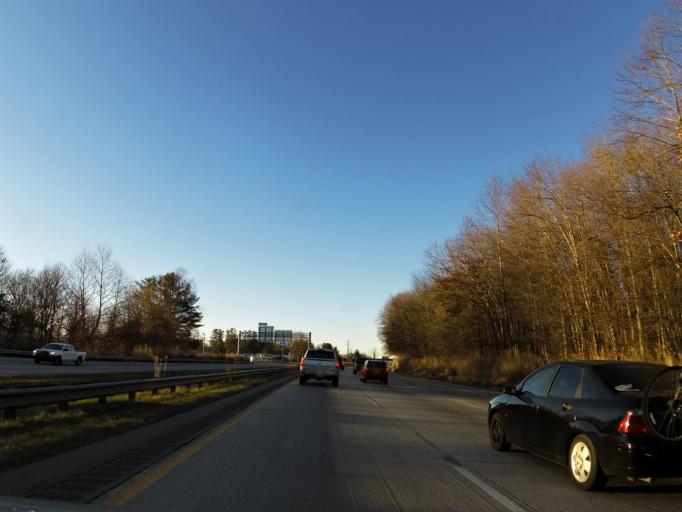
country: US
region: North Carolina
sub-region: Henderson County
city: Fletcher
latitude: 35.4012
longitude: -82.5115
